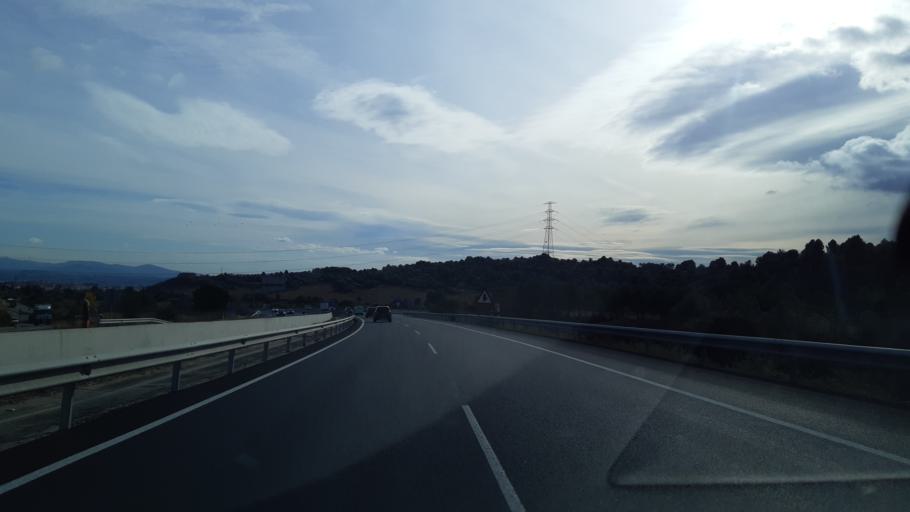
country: ES
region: Catalonia
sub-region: Provincia de Barcelona
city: Collbato
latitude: 41.5575
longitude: 1.8352
